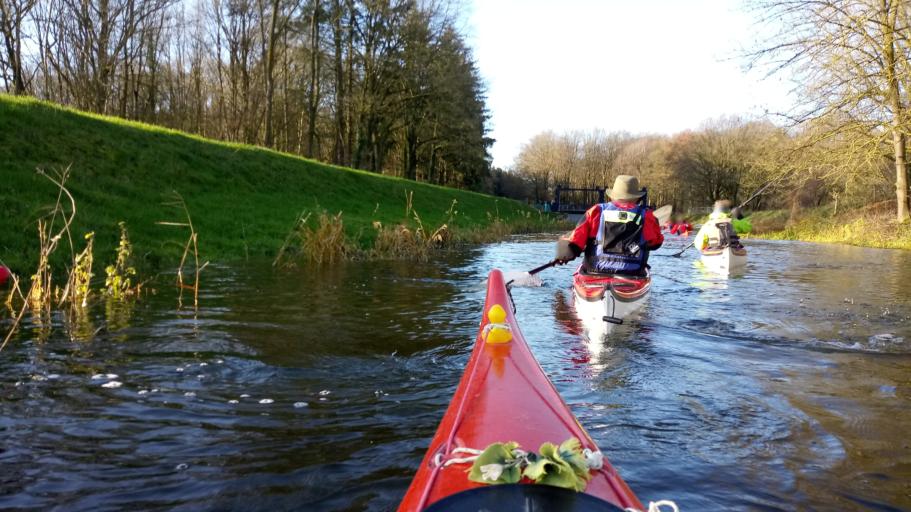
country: NL
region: Gelderland
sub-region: Gemeente Bronckhorst
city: Baak
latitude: 52.0962
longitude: 6.2636
